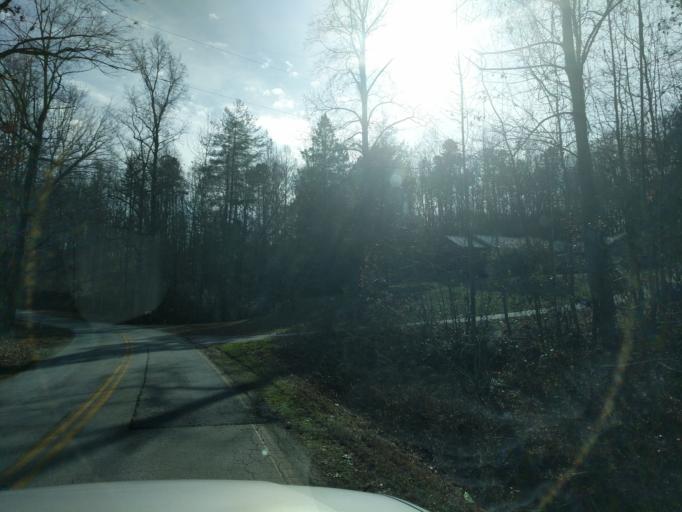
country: US
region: South Carolina
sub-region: Oconee County
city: Walhalla
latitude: 34.8370
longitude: -83.0571
